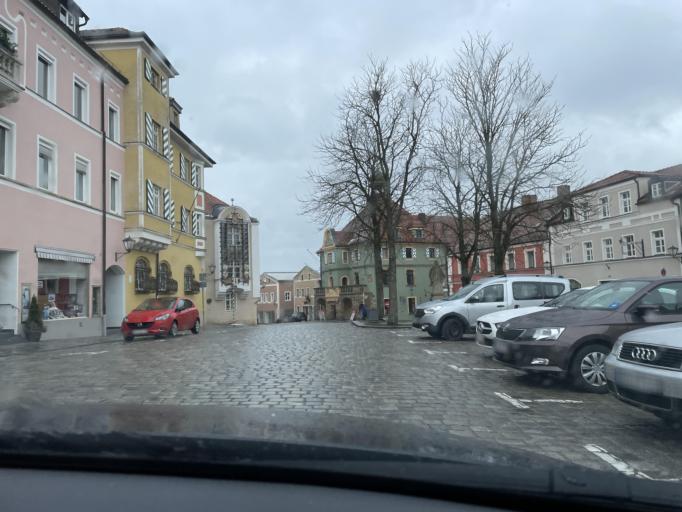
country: DE
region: Bavaria
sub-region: Upper Palatinate
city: Furth im Wald
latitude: 49.3084
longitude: 12.8443
